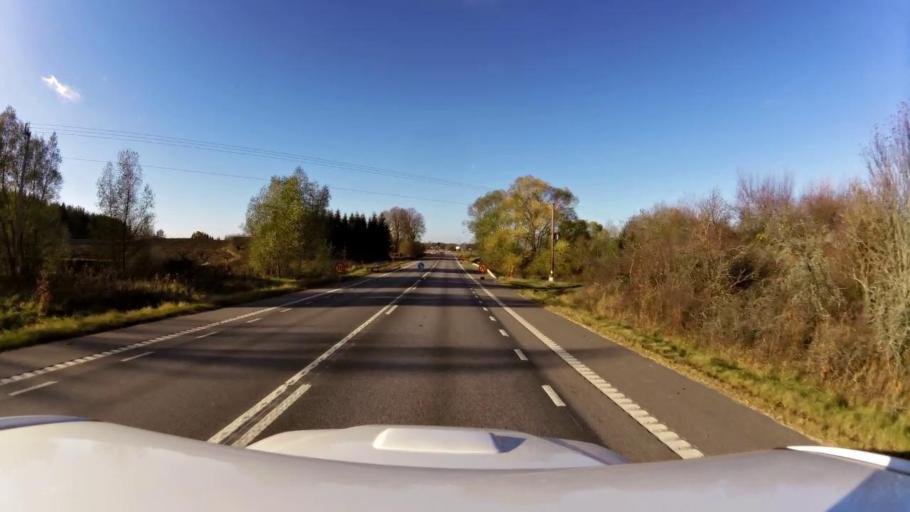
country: SE
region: OEstergoetland
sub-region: Linkopings Kommun
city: Linghem
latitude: 58.4372
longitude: 15.7631
